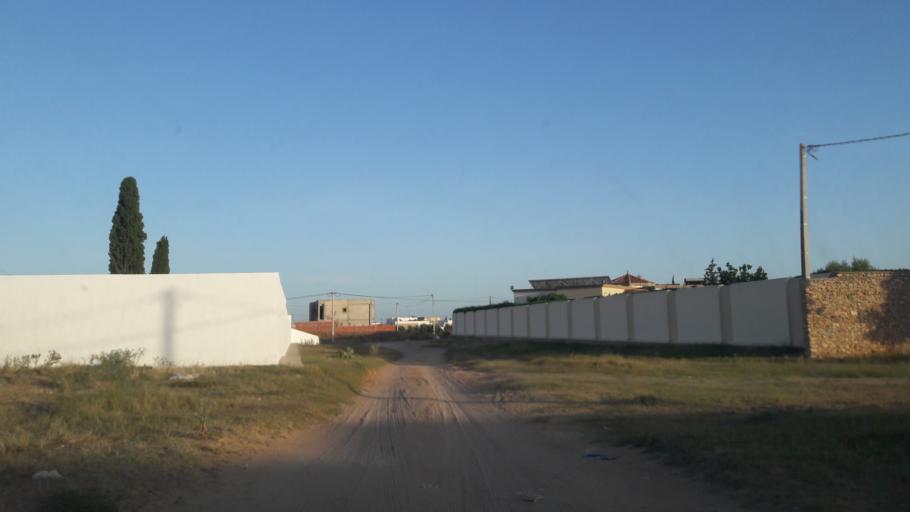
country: TN
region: Safaqis
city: Al Qarmadah
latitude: 34.8200
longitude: 10.7486
